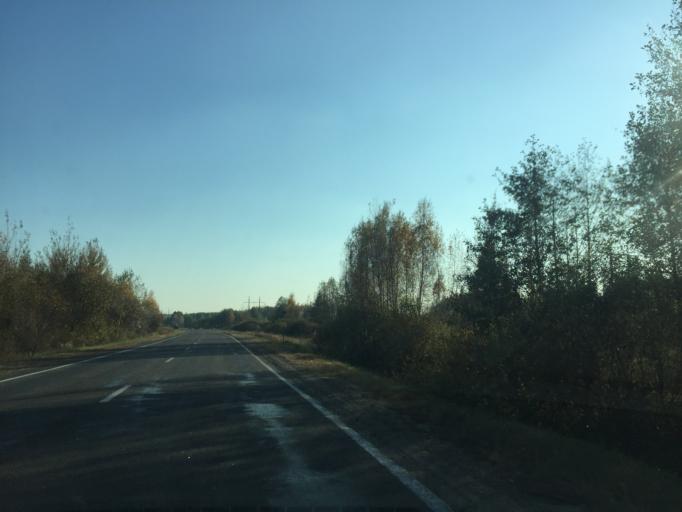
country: BY
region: Gomel
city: Dobrush
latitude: 52.3475
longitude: 31.2296
